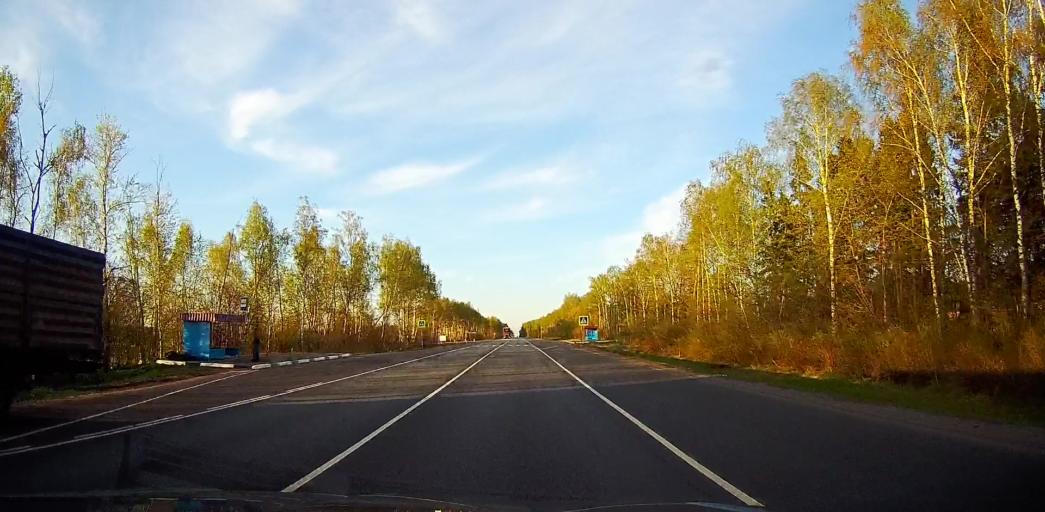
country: RU
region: Moskovskaya
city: Meshcherino
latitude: 55.2426
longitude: 38.4325
